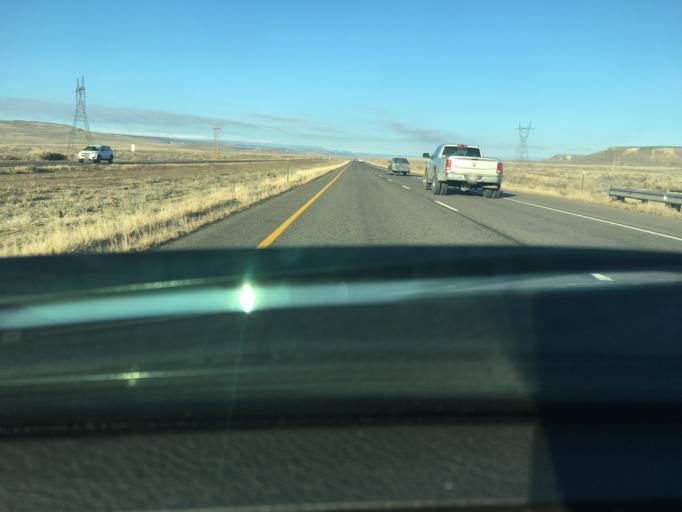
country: US
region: Colorado
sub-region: Delta County
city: Delta
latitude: 38.7594
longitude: -108.1893
